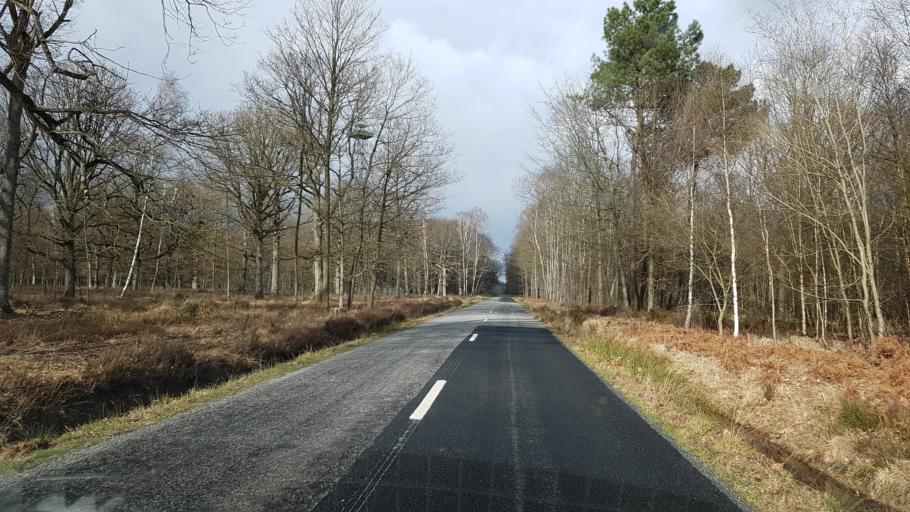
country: FR
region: Ile-de-France
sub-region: Departement des Yvelines
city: Saint-Arnoult-en-Yvelines
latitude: 48.6258
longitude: 1.9259
